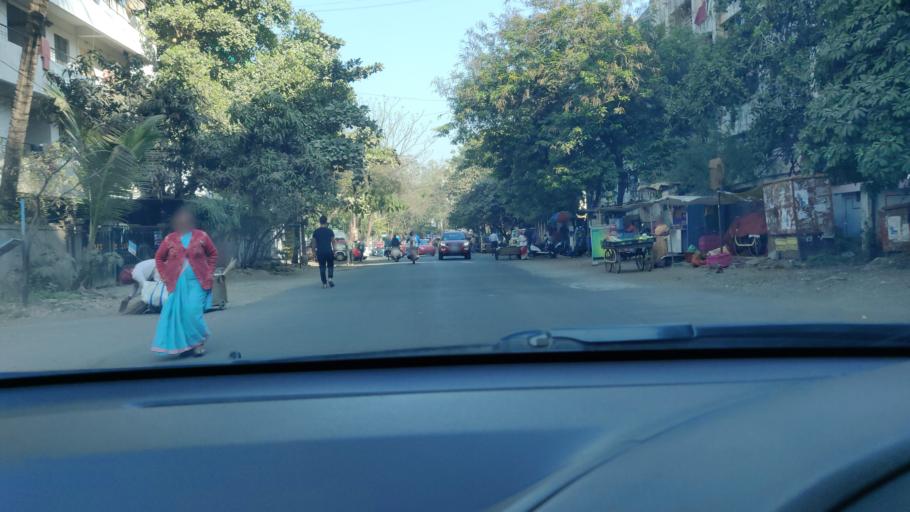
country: IN
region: Maharashtra
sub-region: Pune Division
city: Khadki
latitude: 18.5643
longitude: 73.8025
